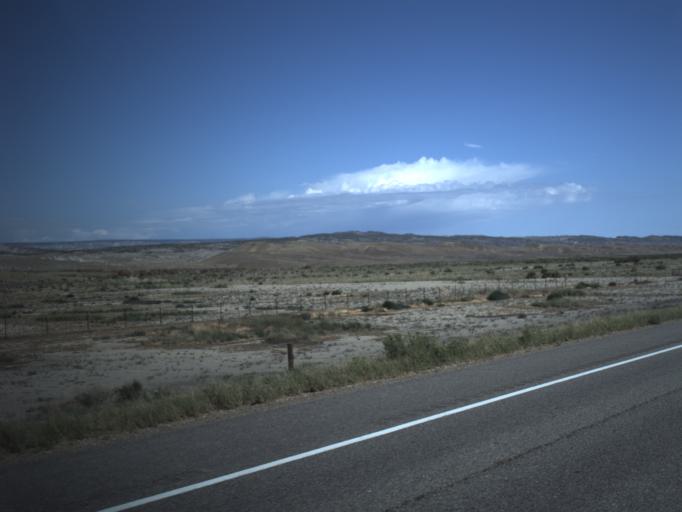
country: US
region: Utah
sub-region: Carbon County
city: East Carbon City
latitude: 39.0959
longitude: -110.3222
